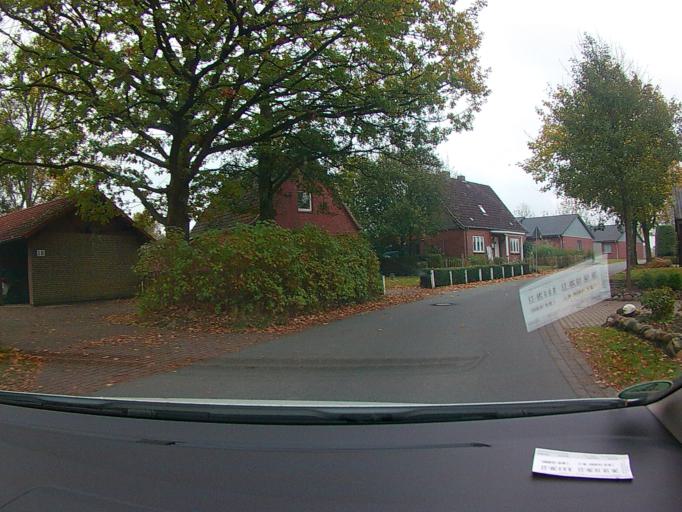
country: DE
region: Schleswig-Holstein
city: Breklum
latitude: 54.6121
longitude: 8.9879
